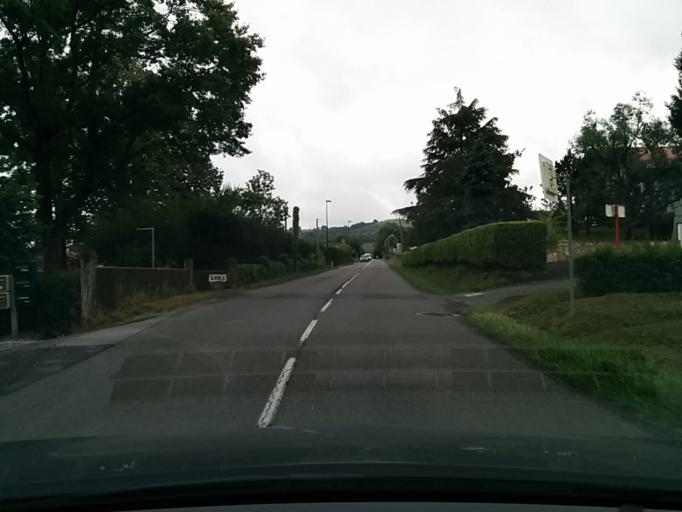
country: FR
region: Aquitaine
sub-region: Departement des Pyrenees-Atlantiques
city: Saint-Pee-sur-Nivelle
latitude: 43.3421
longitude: -1.5486
